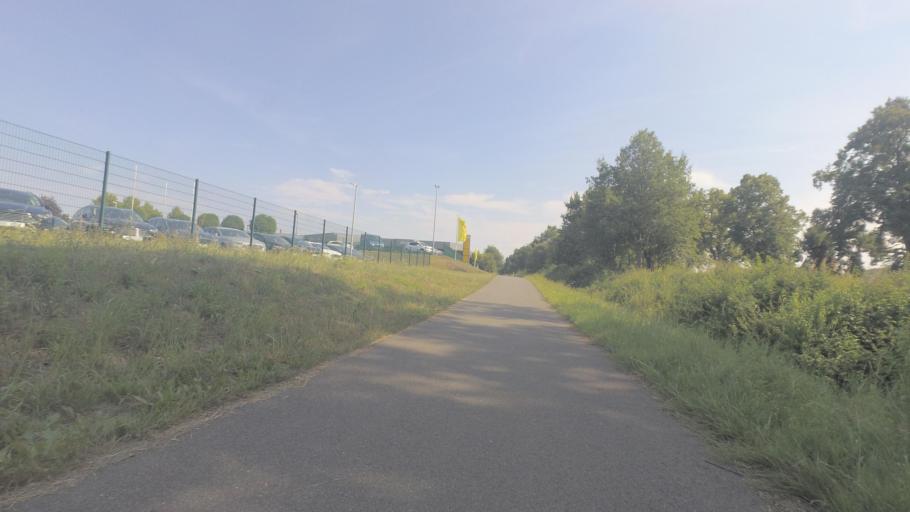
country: DE
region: Mecklenburg-Vorpommern
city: Grimmen
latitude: 54.1064
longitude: 13.0614
